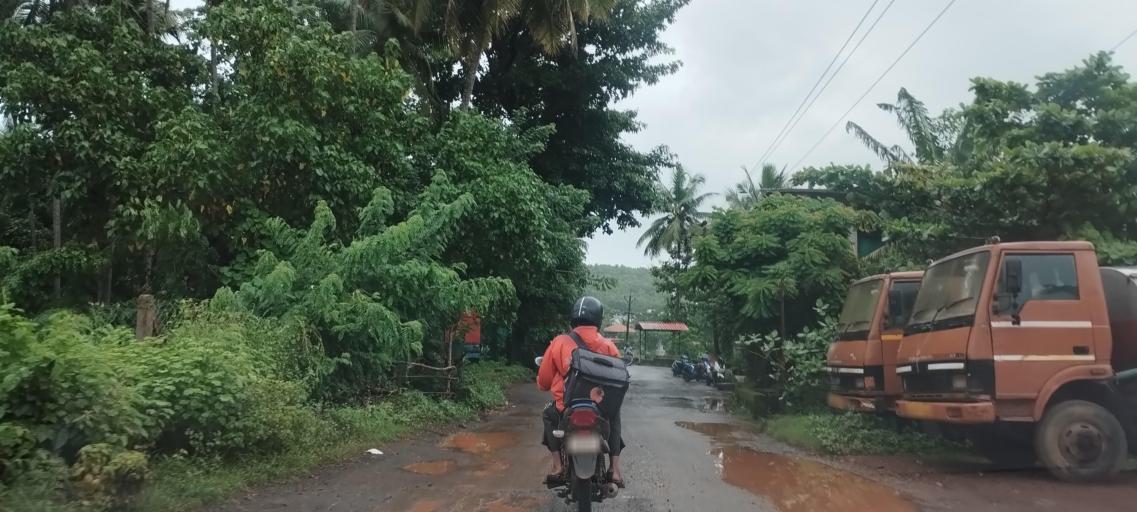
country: IN
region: Goa
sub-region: North Goa
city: Solim
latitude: 15.5947
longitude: 73.7723
